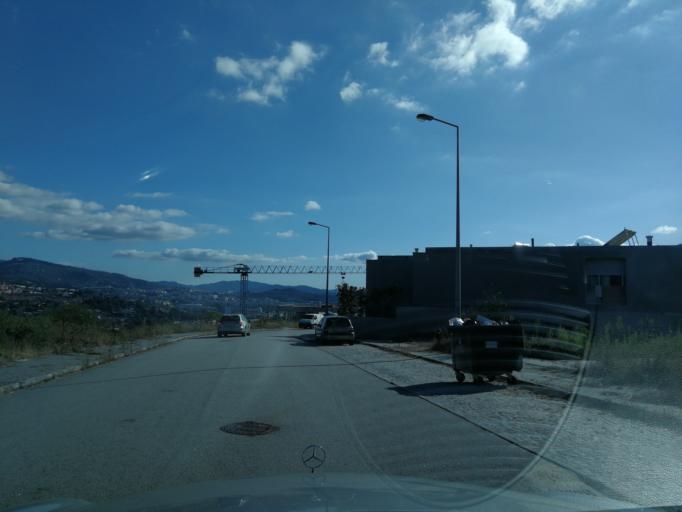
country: PT
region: Braga
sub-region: Braga
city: Adaufe
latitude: 41.5729
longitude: -8.3849
